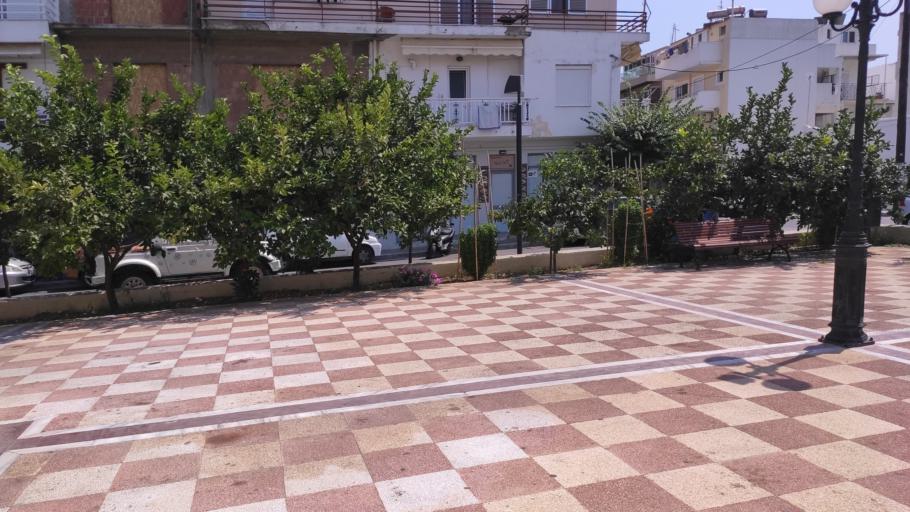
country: GR
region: South Aegean
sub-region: Nomos Dodekanisou
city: Kos
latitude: 36.8989
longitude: 27.2852
